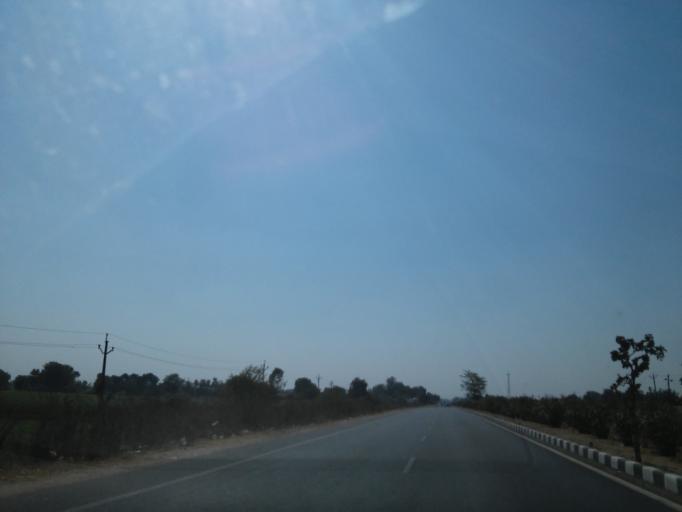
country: IN
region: Gujarat
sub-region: Gandhinagar
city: Chhala
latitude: 23.3815
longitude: 72.8094
